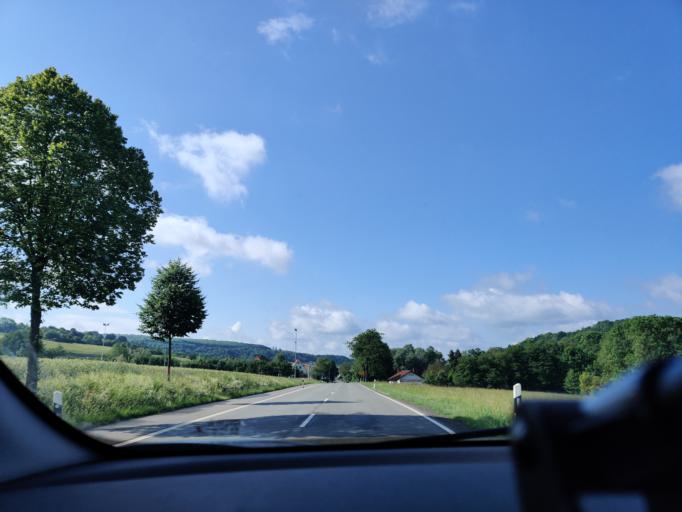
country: DE
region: Saarland
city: Gersheim
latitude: 49.1764
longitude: 7.1618
